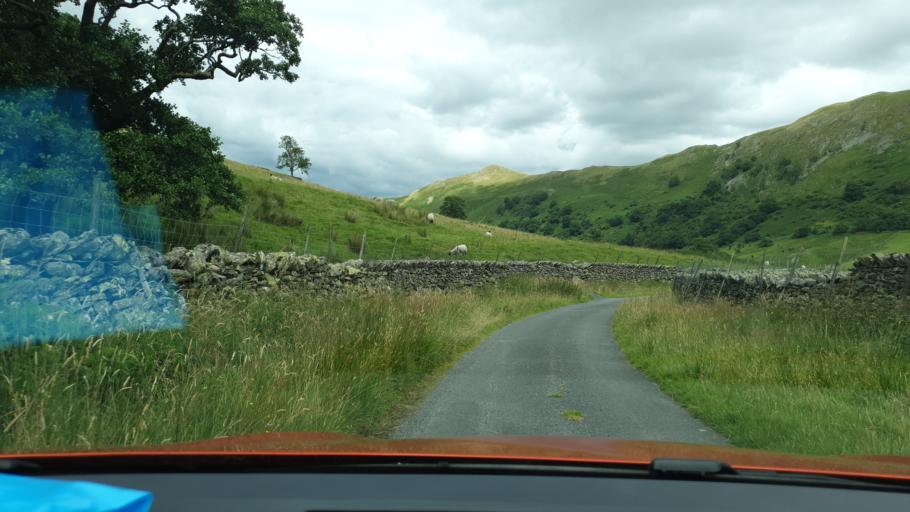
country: GB
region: England
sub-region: Cumbria
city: Ambleside
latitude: 54.5412
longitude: -2.8769
